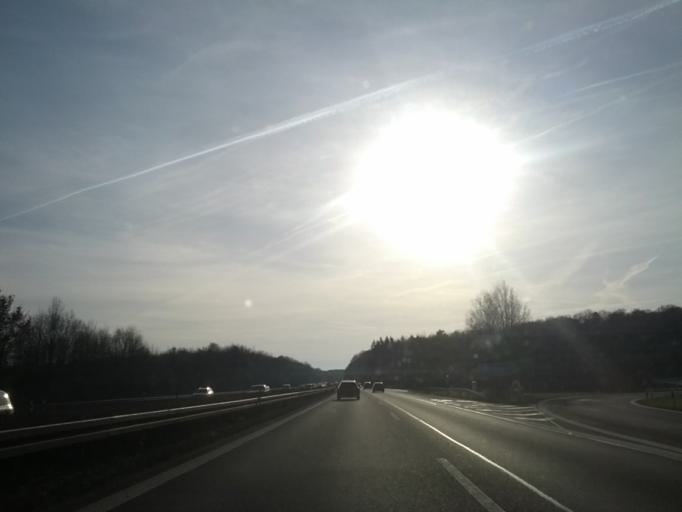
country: DE
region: Bavaria
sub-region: Regierungsbezirk Unterfranken
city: Unterpleichfeld
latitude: 49.9122
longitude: 9.9977
